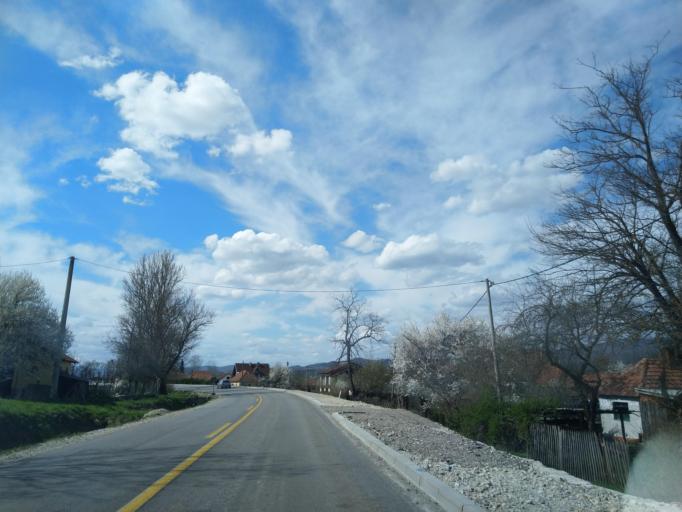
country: RS
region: Central Serbia
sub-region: Zlatiborski Okrug
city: Pozega
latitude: 43.8301
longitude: 20.0748
